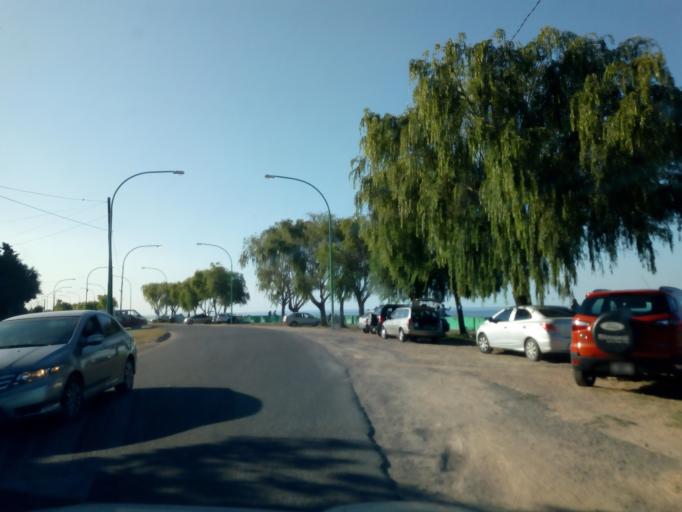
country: AR
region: Buenos Aires
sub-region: Partido de Ensenada
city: Ensenada
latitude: -34.8024
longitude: -57.9860
